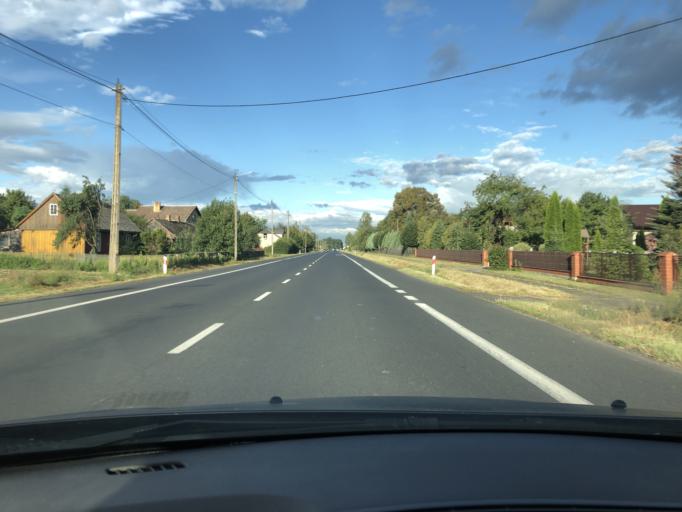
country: PL
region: Lodz Voivodeship
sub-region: Powiat wieruszowski
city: Sokolniki
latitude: 51.3039
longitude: 18.2944
